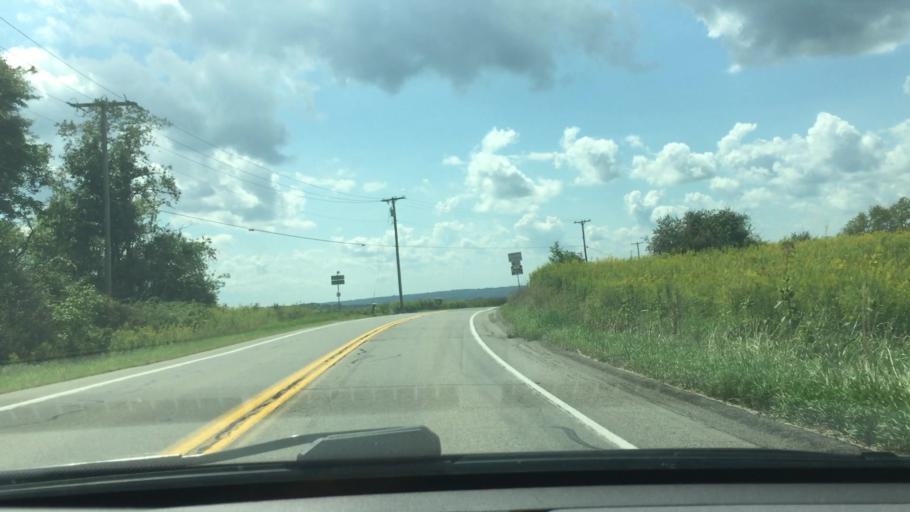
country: US
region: Pennsylvania
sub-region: Lawrence County
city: New Wilmington
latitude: 41.1173
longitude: -80.2438
